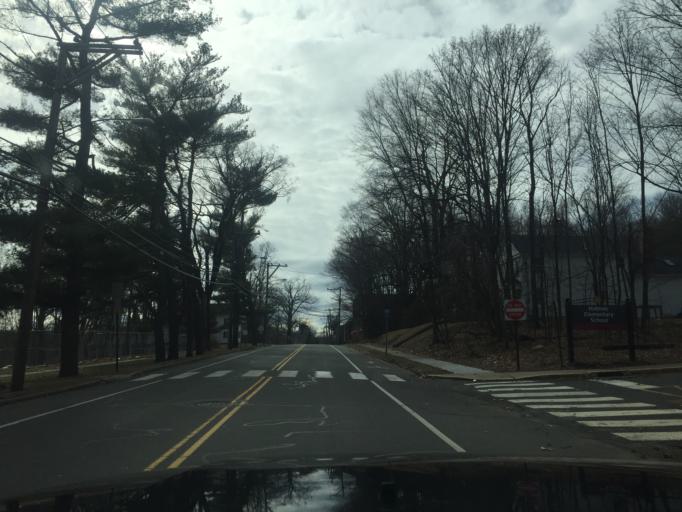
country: US
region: Connecticut
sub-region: Hartford County
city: New Britain
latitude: 41.7043
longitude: -72.7758
